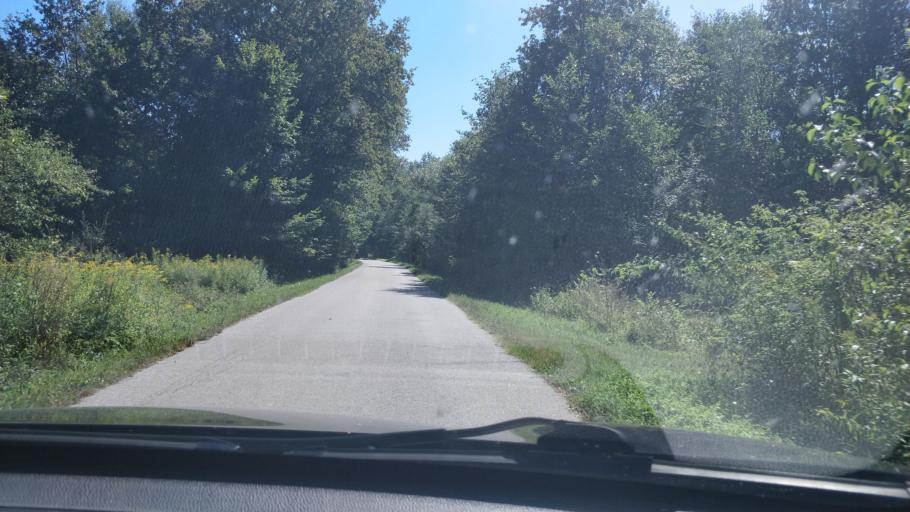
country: HR
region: Karlovacka
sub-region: Grad Karlovac
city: Karlovac
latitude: 45.4686
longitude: 15.6635
